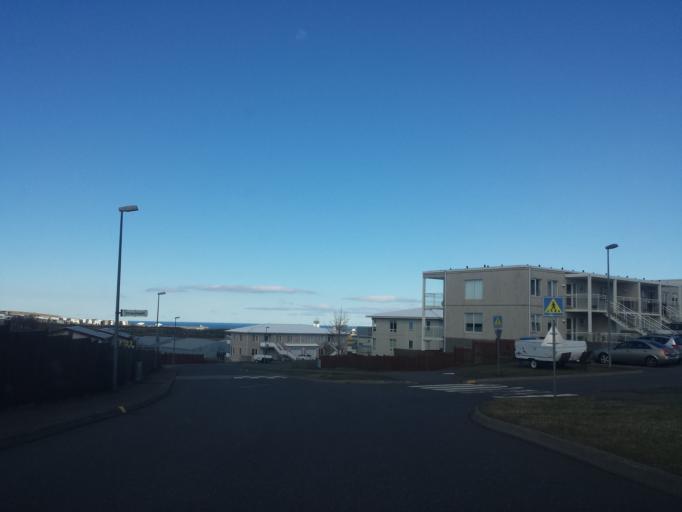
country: IS
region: Capital Region
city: Reykjavik
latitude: 64.0904
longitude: -21.8511
